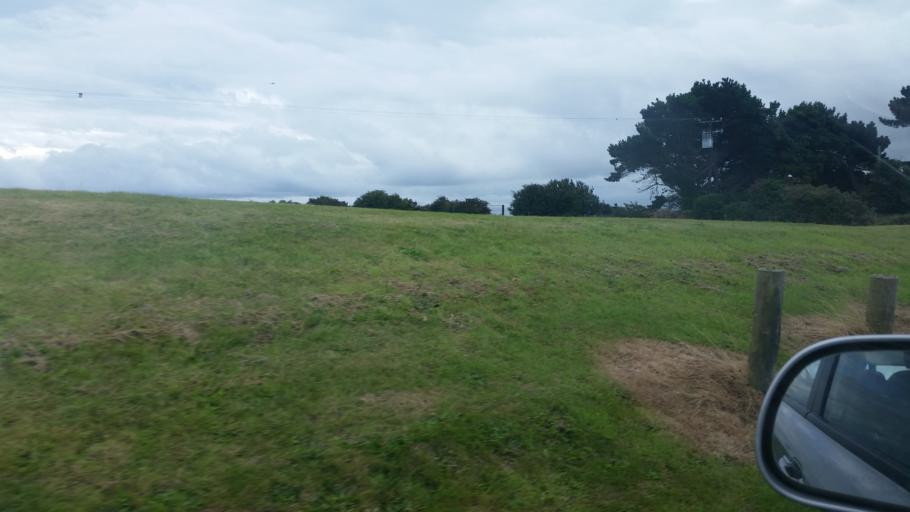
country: IE
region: Leinster
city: Portmarnock
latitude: 53.4159
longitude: -6.1282
